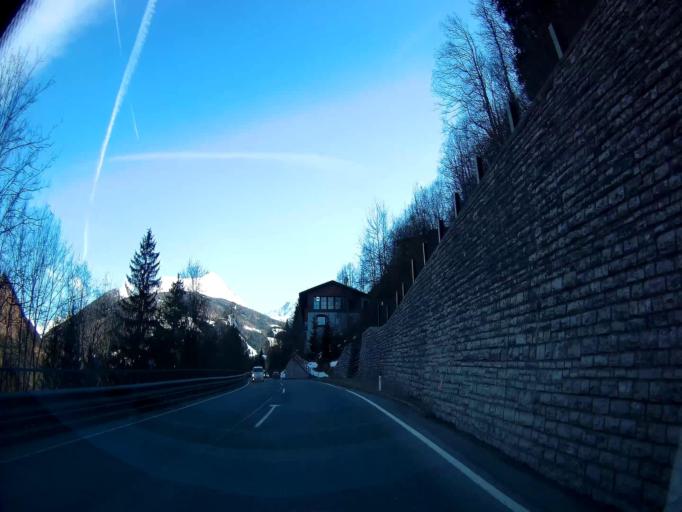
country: AT
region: Salzburg
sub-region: Politischer Bezirk Sankt Johann im Pongau
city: Bad Gastein
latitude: 47.1350
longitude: 13.1269
